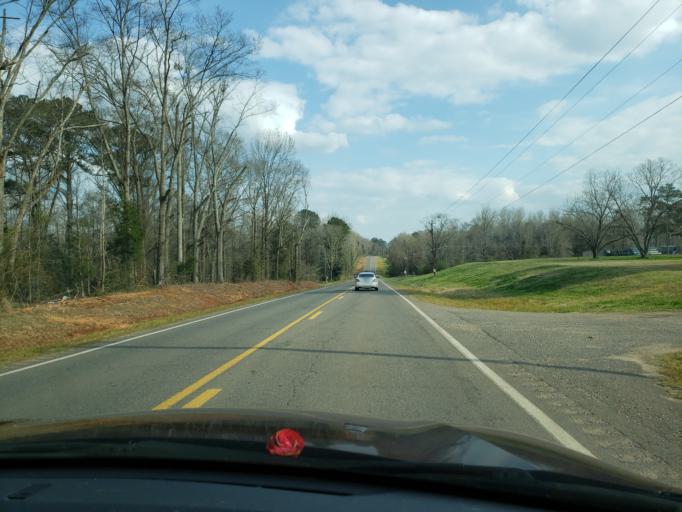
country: US
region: Alabama
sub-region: Hale County
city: Greensboro
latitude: 32.7128
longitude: -87.6144
